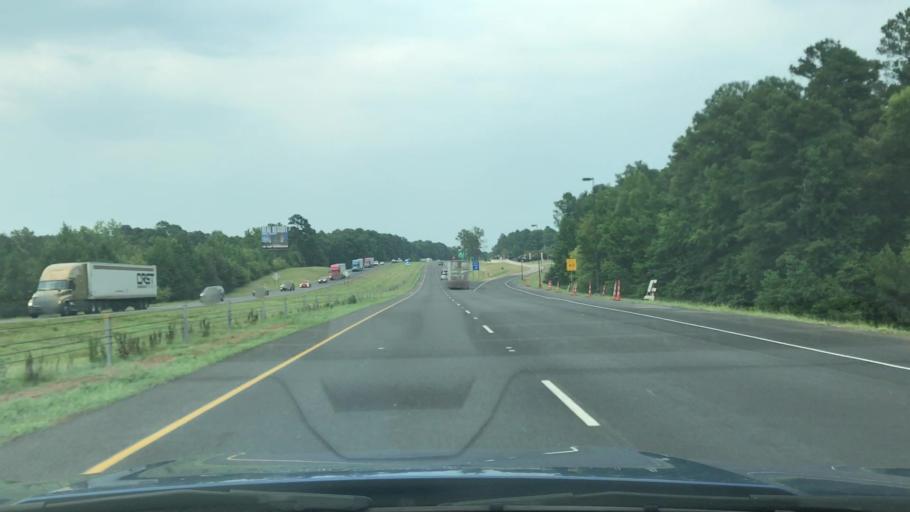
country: US
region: Louisiana
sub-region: Caddo Parish
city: Greenwood
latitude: 32.4516
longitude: -94.0070
